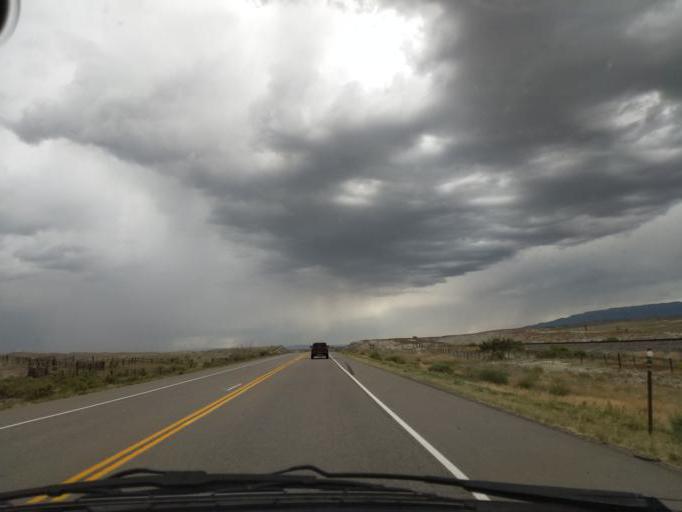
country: US
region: Colorado
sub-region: Delta County
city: Orchard City
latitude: 38.8024
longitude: -107.8912
